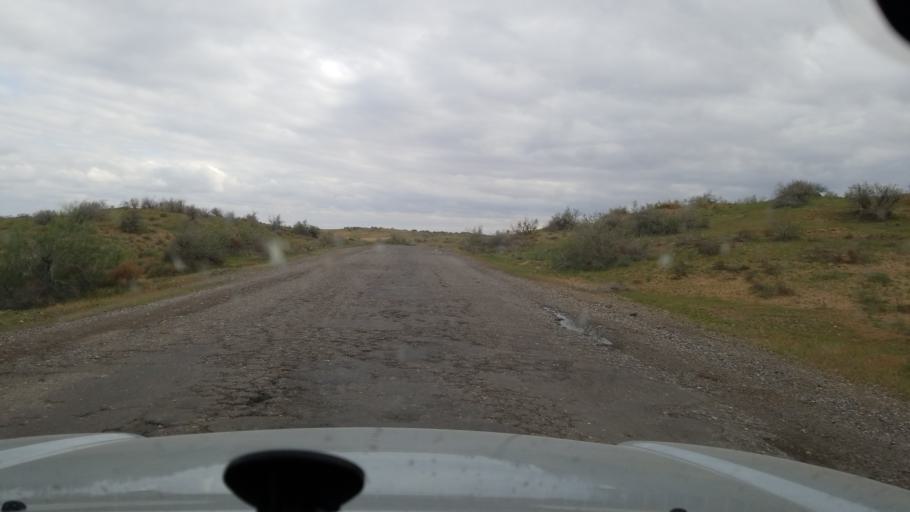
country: TM
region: Mary
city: Serhetabat
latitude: 36.0478
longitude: 62.6168
